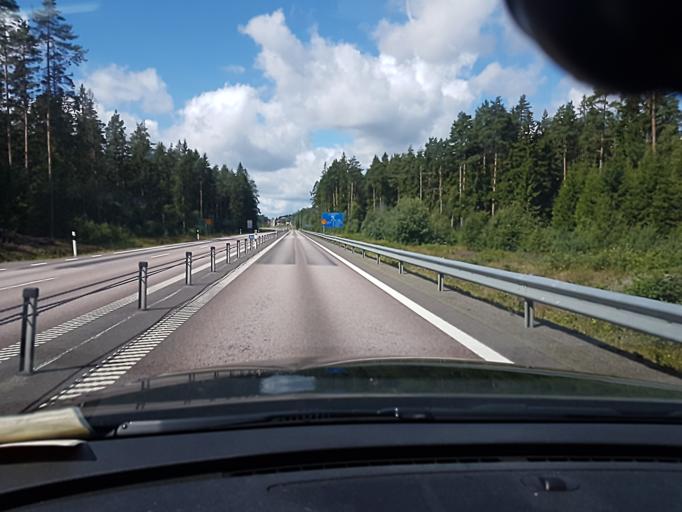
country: SE
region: Kalmar
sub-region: Emmaboda Kommun
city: Emmaboda
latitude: 56.7357
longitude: 15.4941
